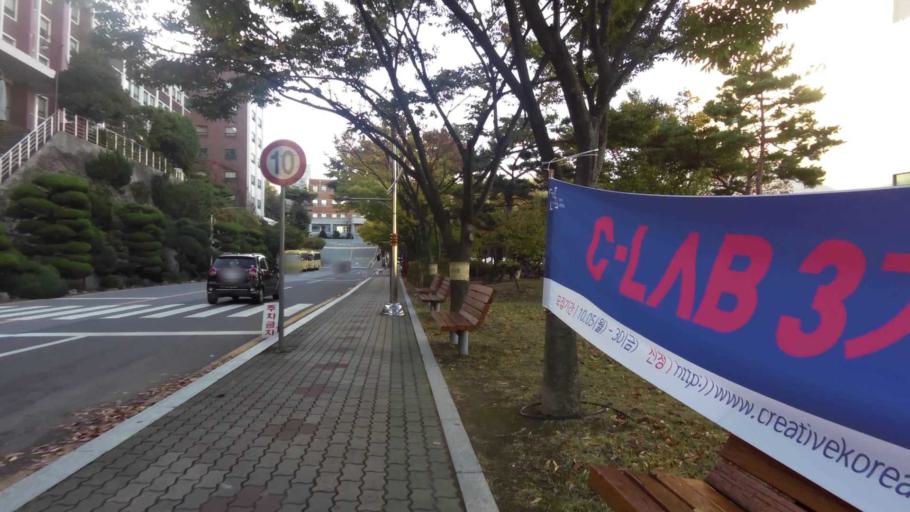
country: KR
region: Daegu
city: Daegu
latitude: 35.8542
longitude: 128.6477
